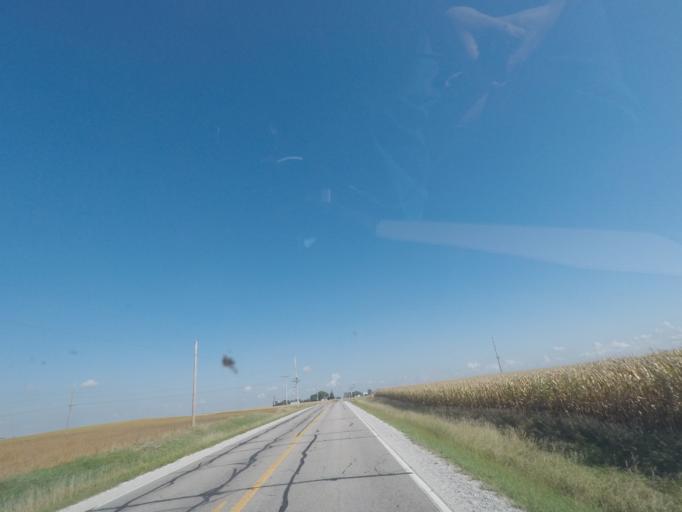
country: US
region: Iowa
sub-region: Story County
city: Nevada
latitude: 42.0333
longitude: -93.4058
